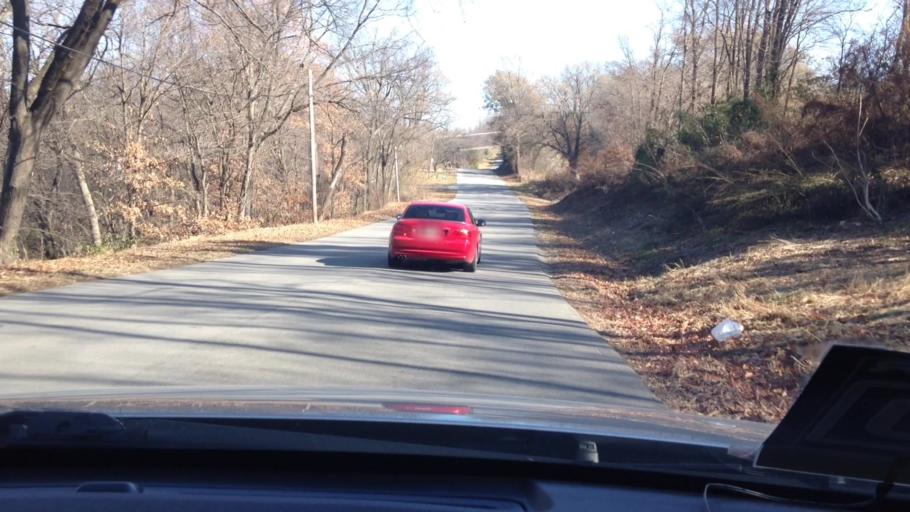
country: US
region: Missouri
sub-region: Platte County
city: Weston
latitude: 39.4174
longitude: -94.8944
